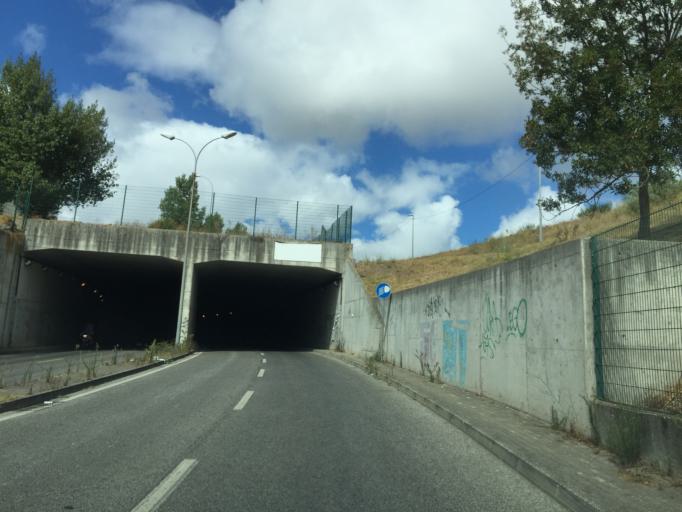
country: PT
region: Lisbon
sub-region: Amadora
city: Amadora
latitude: 38.7726
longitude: -9.2267
